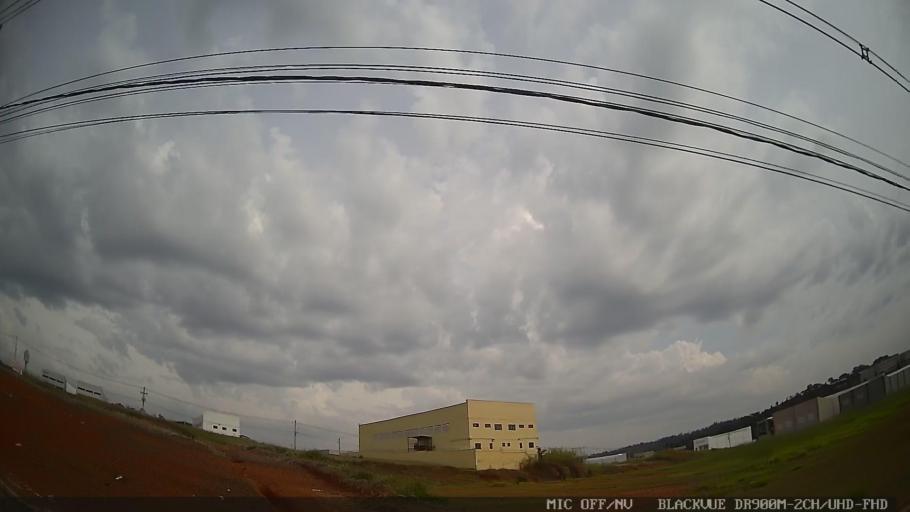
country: BR
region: Sao Paulo
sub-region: Indaiatuba
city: Indaiatuba
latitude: -23.1209
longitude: -47.2687
